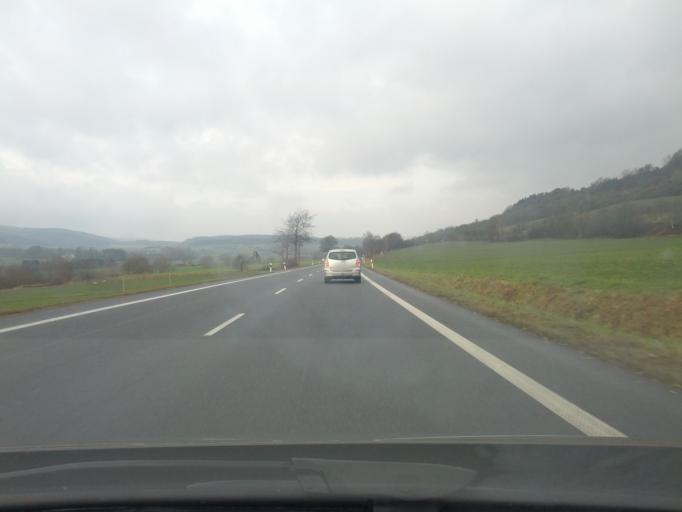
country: DE
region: Hesse
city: Witzenhausen
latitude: 51.3641
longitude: 9.8203
